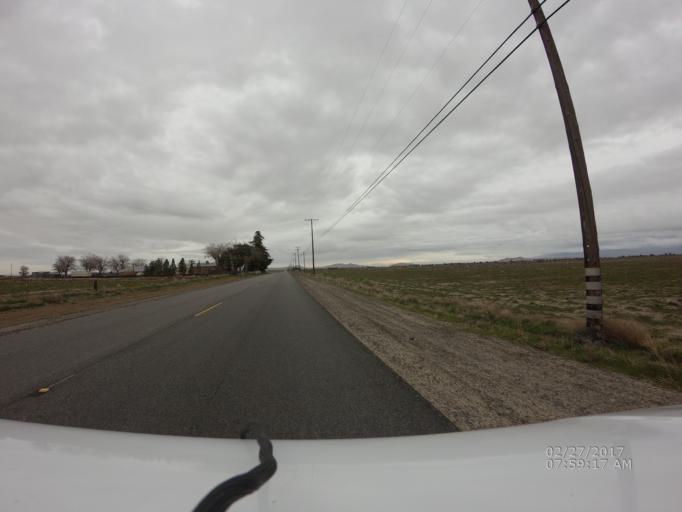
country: US
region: California
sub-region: Los Angeles County
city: Lancaster
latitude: 34.7048
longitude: -117.9895
